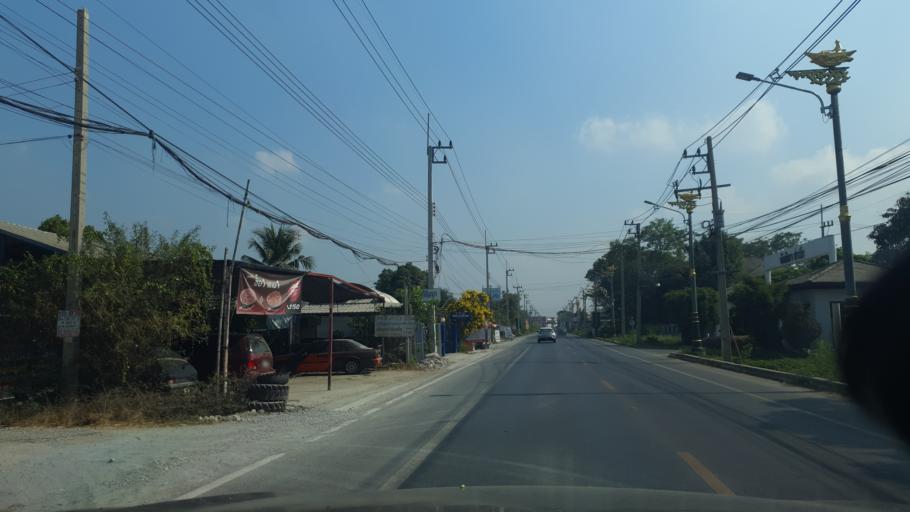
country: TH
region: Nakhon Pathom
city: Salaya
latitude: 13.7744
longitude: 100.2967
